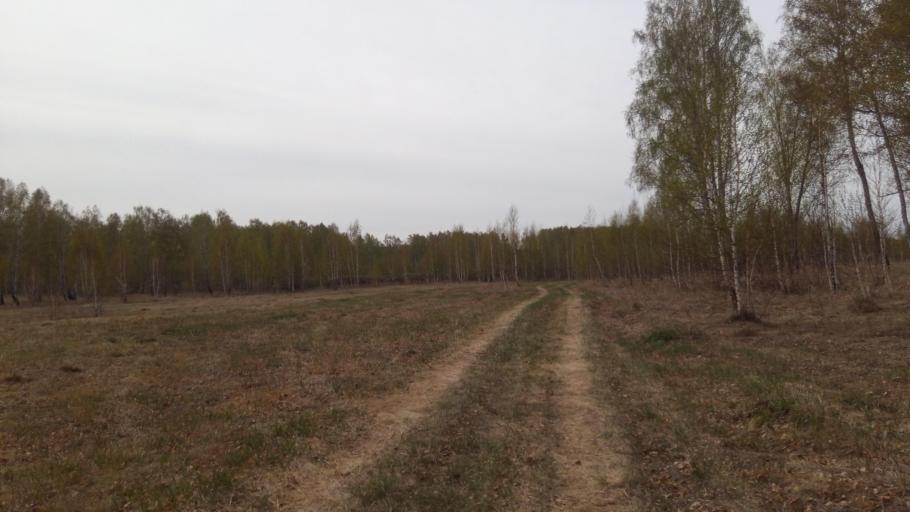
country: RU
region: Chelyabinsk
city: Timiryazevskiy
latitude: 55.0080
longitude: 60.8588
